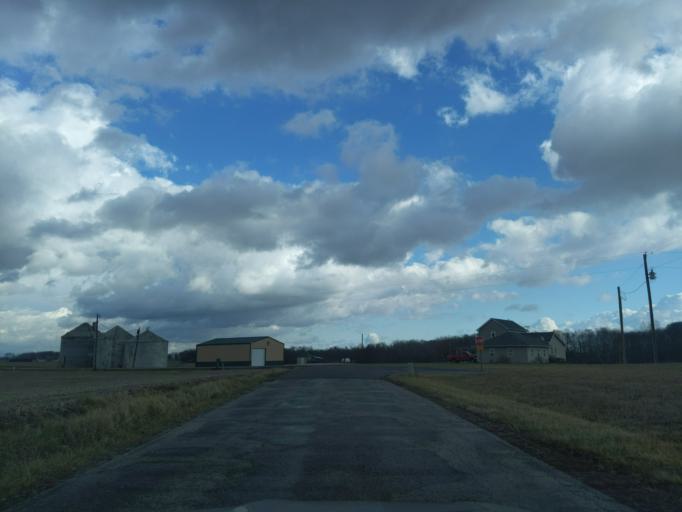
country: US
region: Indiana
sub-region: Decatur County
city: Greensburg
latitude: 39.4133
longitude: -85.5131
